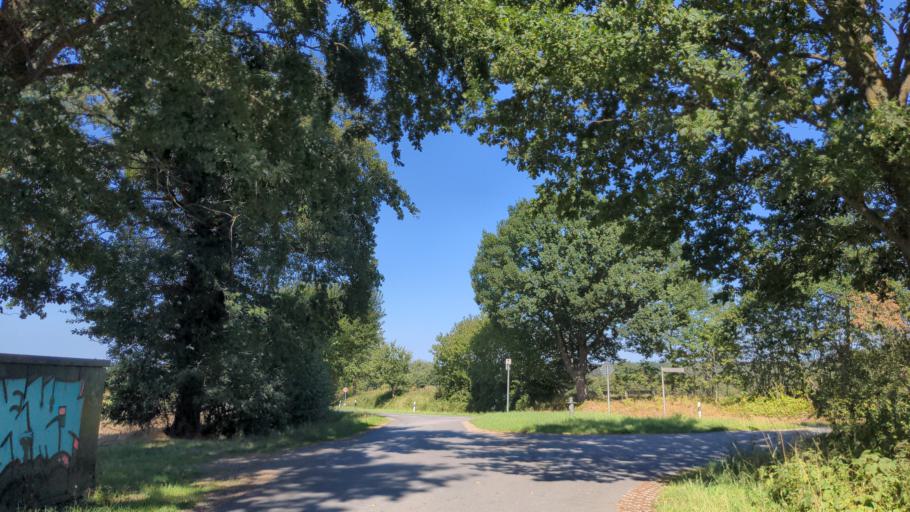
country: DE
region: Schleswig-Holstein
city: Klempau
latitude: 53.7653
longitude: 10.6745
